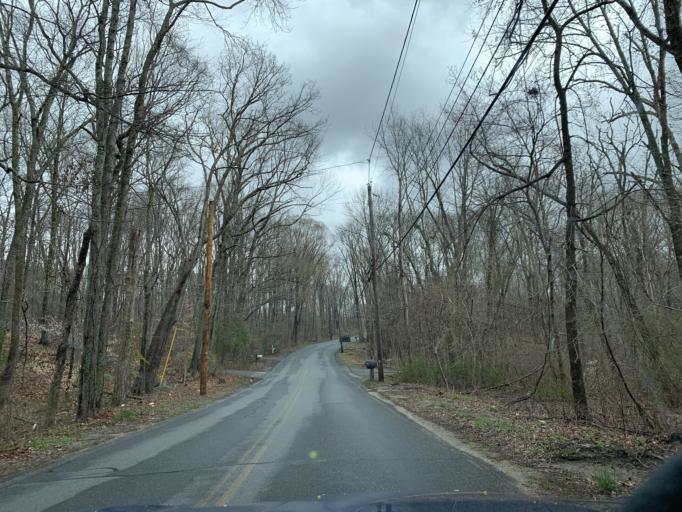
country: US
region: Massachusetts
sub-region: Bristol County
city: Rehoboth
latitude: 41.8744
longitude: -71.2076
